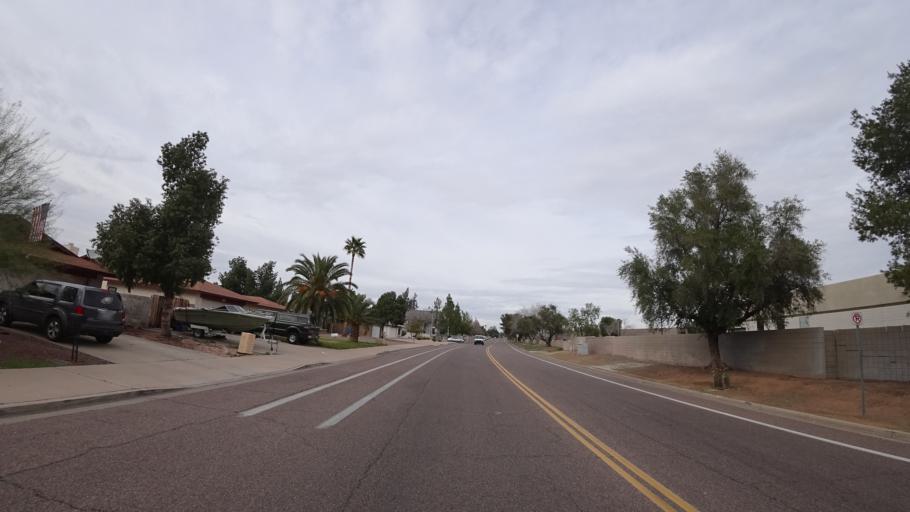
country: US
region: Arizona
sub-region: Maricopa County
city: Glendale
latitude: 33.6298
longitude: -112.1212
